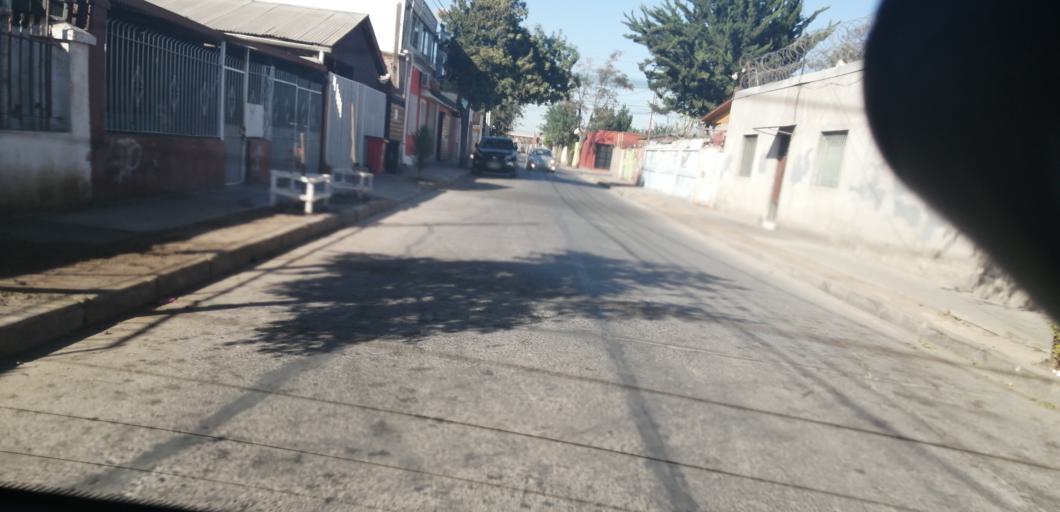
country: CL
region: Santiago Metropolitan
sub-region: Provincia de Santiago
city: Lo Prado
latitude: -33.4322
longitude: -70.7679
